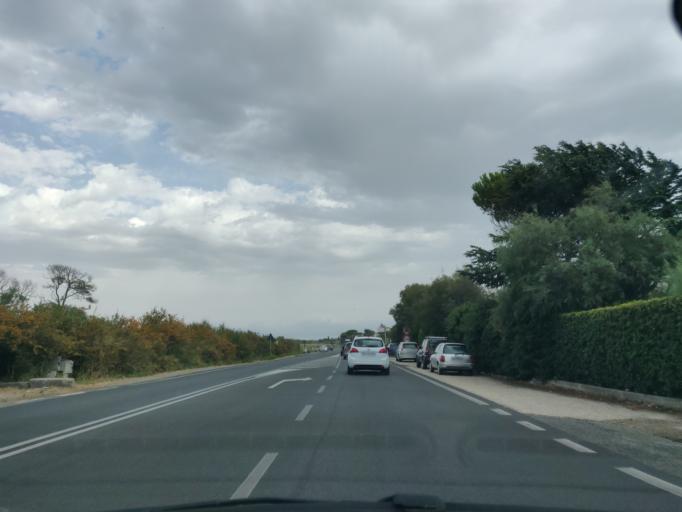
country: IT
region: Latium
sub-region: Citta metropolitana di Roma Capitale
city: Santa Marinella
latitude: 42.0385
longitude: 11.9185
